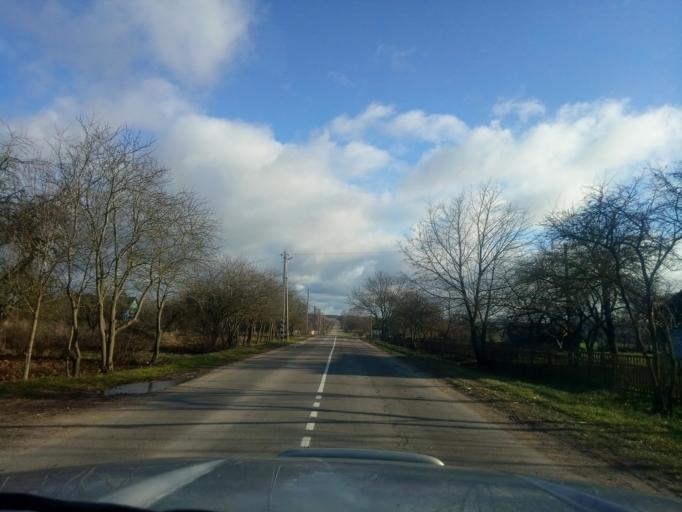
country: BY
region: Minsk
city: Tsimkavichy
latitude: 53.1761
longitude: 26.9460
